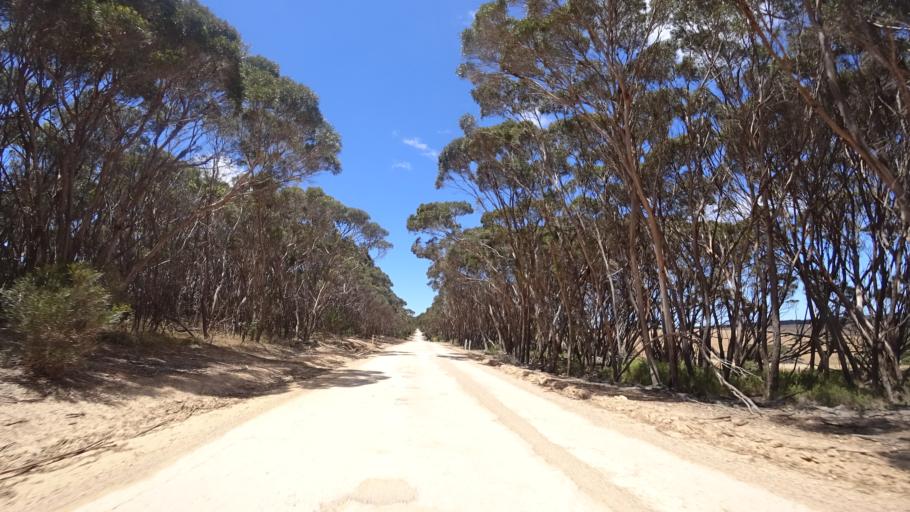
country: AU
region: South Australia
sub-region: Yankalilla
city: Normanville
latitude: -35.8158
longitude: 138.0754
